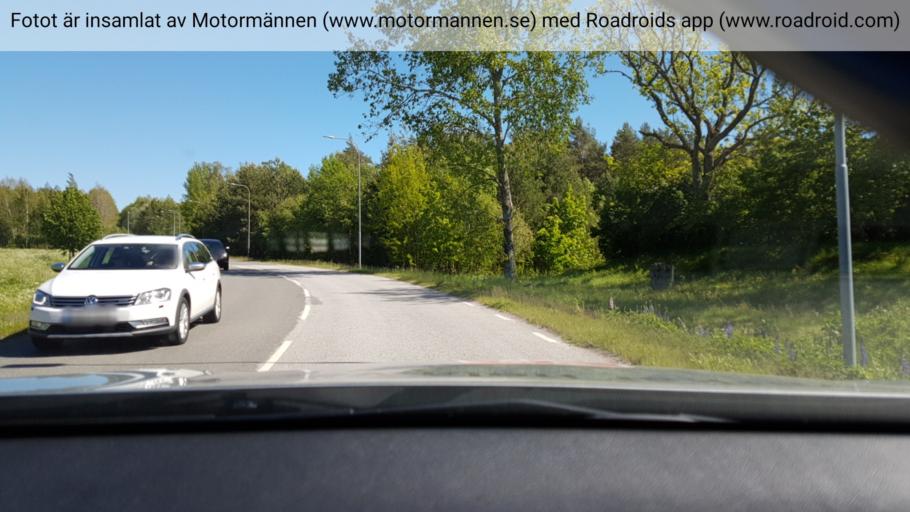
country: SE
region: Vaestra Goetaland
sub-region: Toreboda Kommun
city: Toereboda
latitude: 58.8311
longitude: 13.9866
